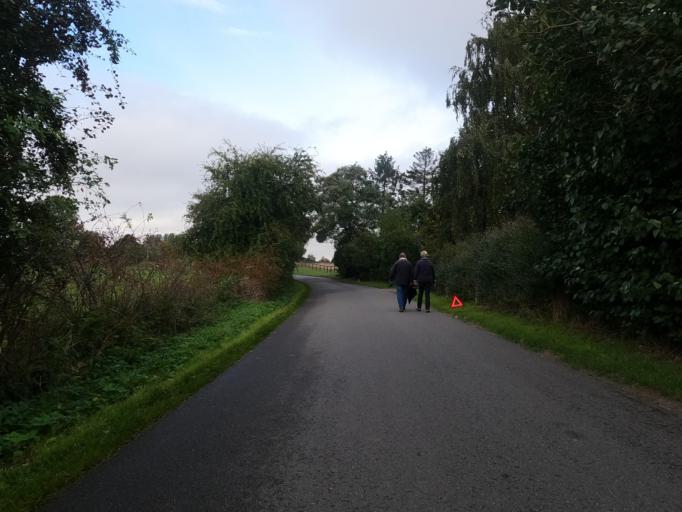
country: DE
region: Schleswig-Holstein
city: Neukirchen
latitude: 54.3077
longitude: 11.0548
